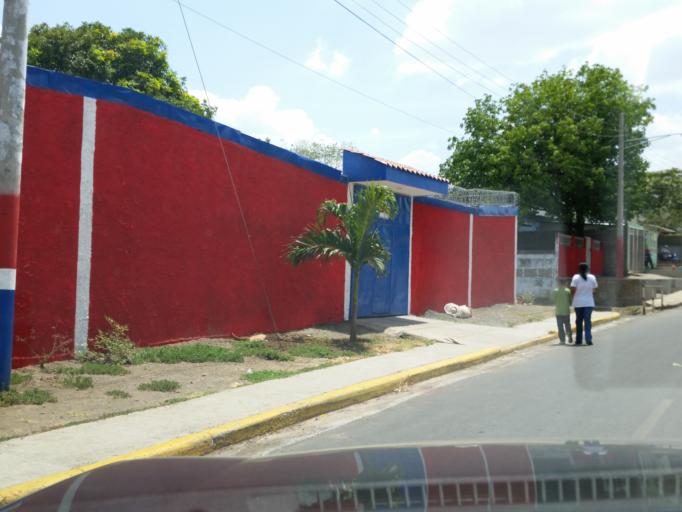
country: NI
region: Managua
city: Managua
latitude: 12.1485
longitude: -86.2163
